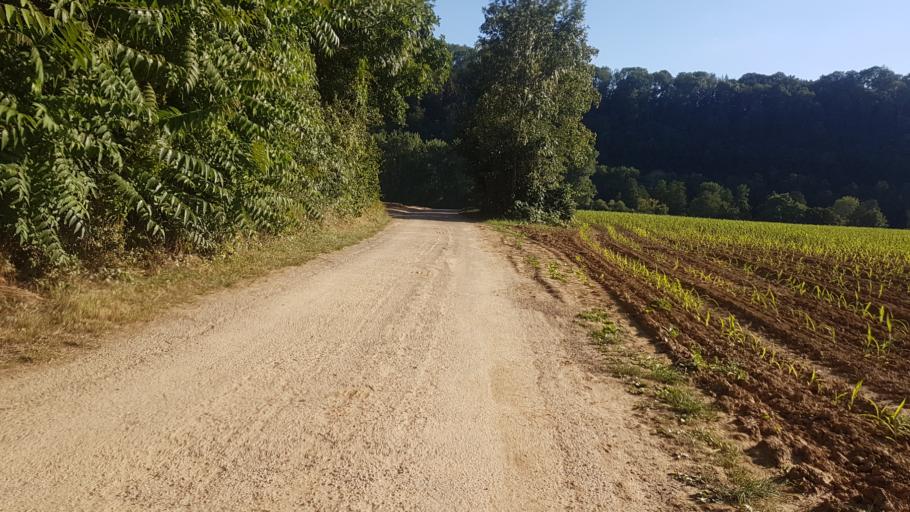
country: DE
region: Baden-Wuerttemberg
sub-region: Regierungsbezirk Stuttgart
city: Mockmuhl
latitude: 49.2933
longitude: 9.3231
